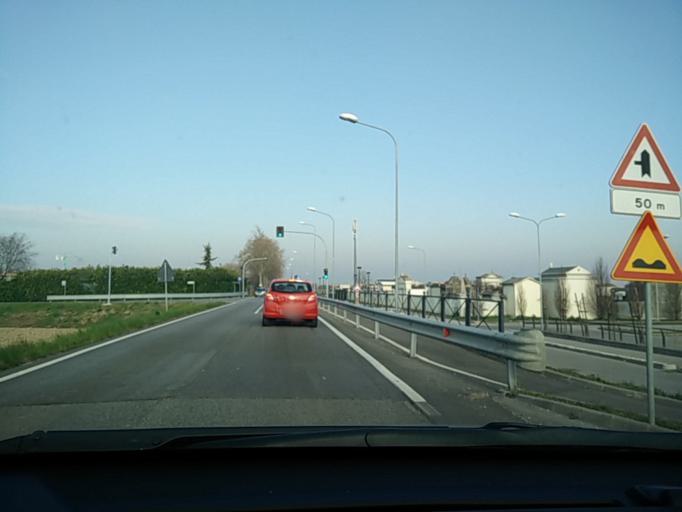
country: IT
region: Veneto
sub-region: Provincia di Treviso
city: Zenson di Piave
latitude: 45.6780
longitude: 12.4857
